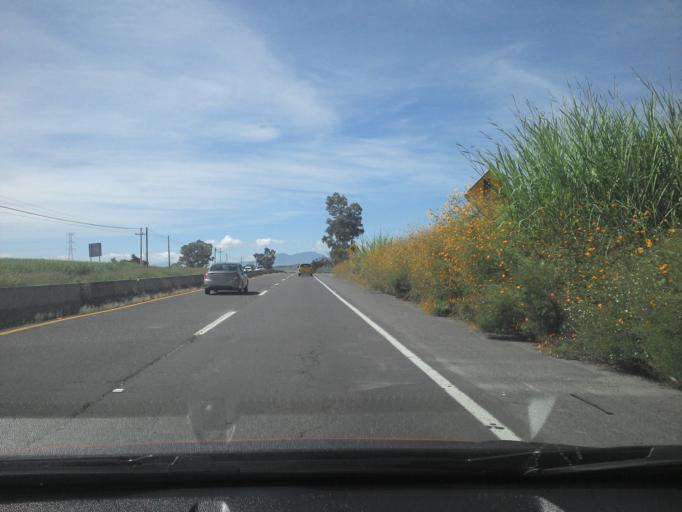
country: MX
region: Jalisco
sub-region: Tala
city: Los Ruisenores
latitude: 20.7094
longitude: -103.6687
